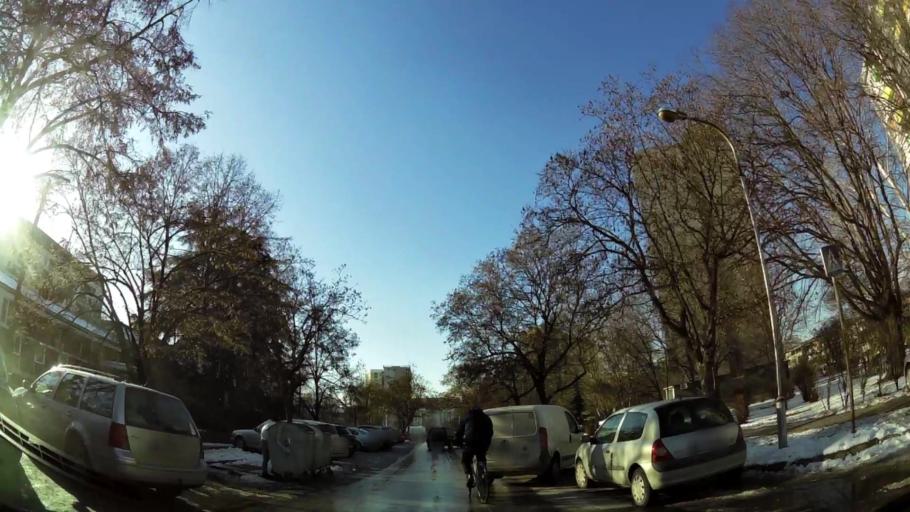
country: MK
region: Karpos
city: Skopje
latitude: 42.0044
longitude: 21.3966
